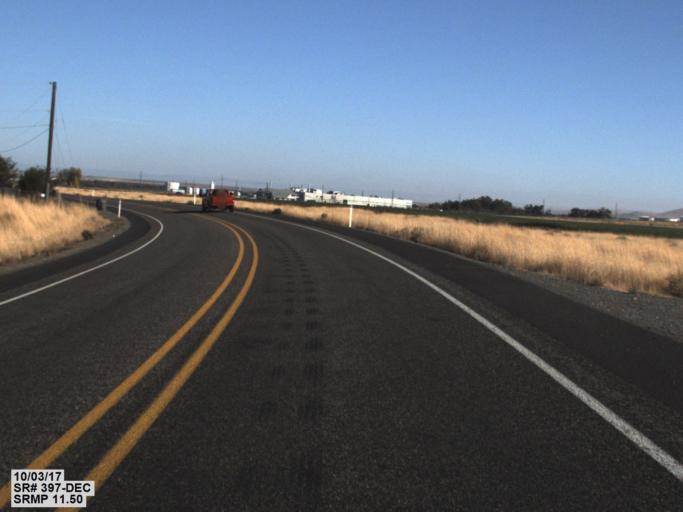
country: US
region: Washington
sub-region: Benton County
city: Finley
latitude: 46.1481
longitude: -119.0215
